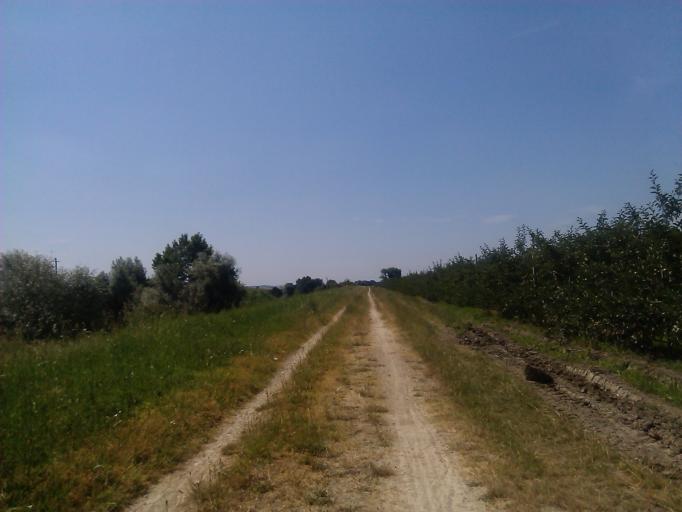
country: IT
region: Tuscany
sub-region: Province of Arezzo
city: Pieve al Toppo
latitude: 43.3744
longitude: 11.8247
